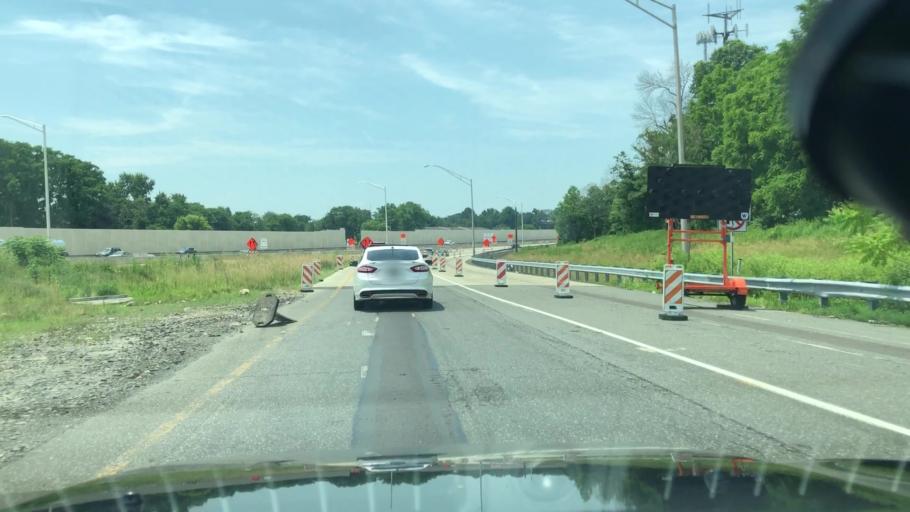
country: US
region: Pennsylvania
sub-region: Bucks County
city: Croydon
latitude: 40.1073
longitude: -74.8957
